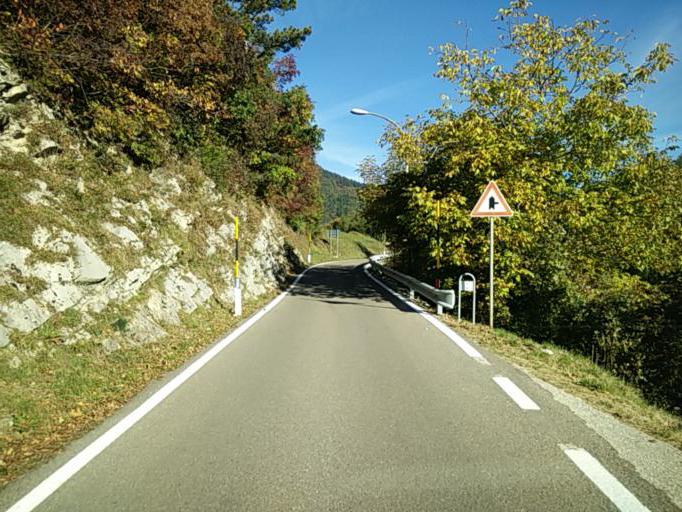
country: IT
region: Trentino-Alto Adige
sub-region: Provincia di Trento
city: Garniga Nuova
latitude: 46.0036
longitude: 11.0860
